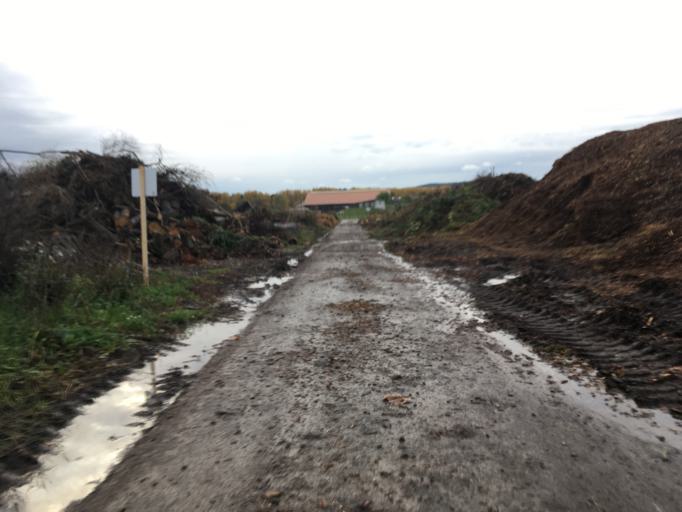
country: DE
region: Baden-Wuerttemberg
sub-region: Regierungsbezirk Stuttgart
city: Nordheim
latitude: 49.1049
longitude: 9.1608
